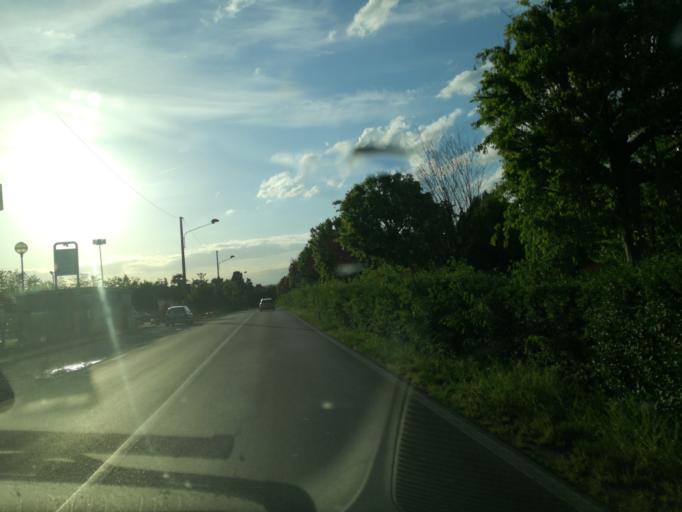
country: IT
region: Lombardy
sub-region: Provincia di Lecco
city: Osnago
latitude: 45.6783
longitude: 9.4001
